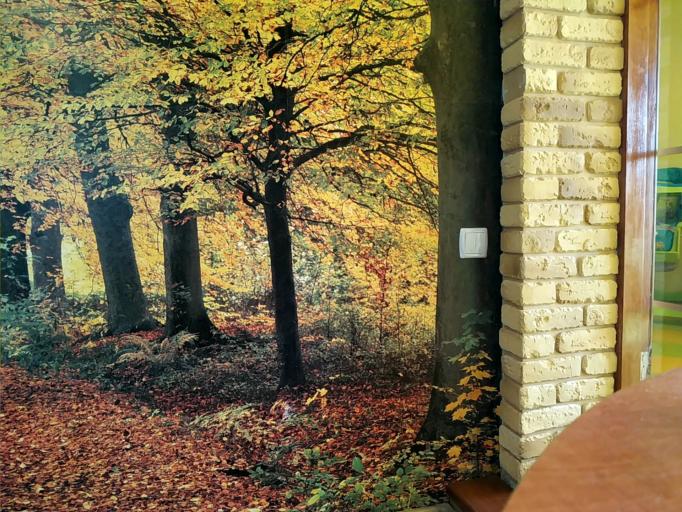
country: RU
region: Novgorod
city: Staraya Russa
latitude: 57.8321
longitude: 31.4868
